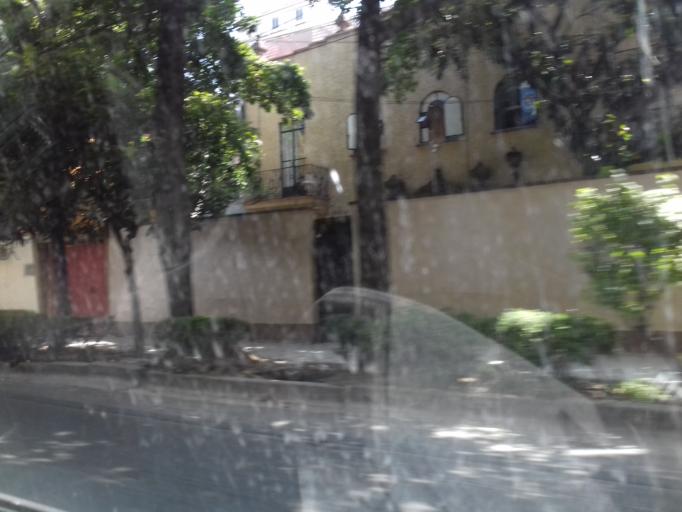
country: MX
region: Mexico City
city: Colonia del Valle
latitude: 19.3678
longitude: -99.1688
